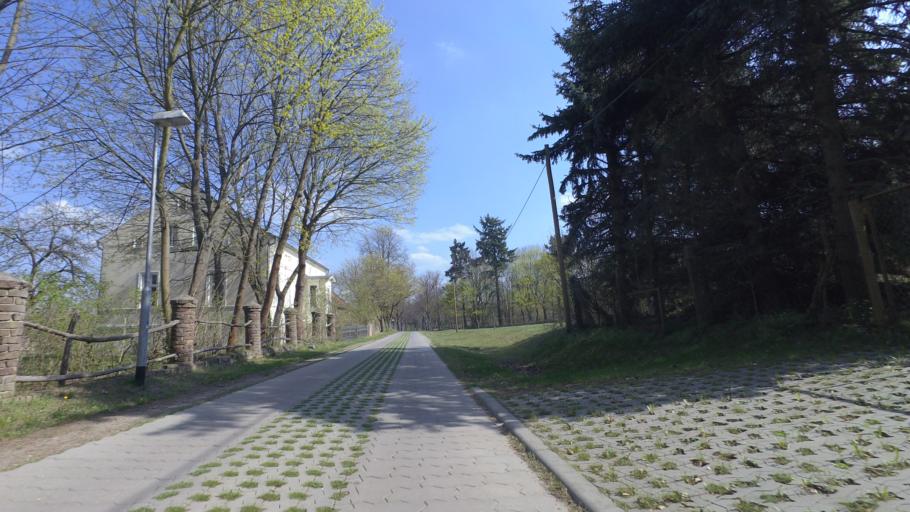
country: DE
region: Brandenburg
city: Teupitz
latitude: 52.1775
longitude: 13.5661
